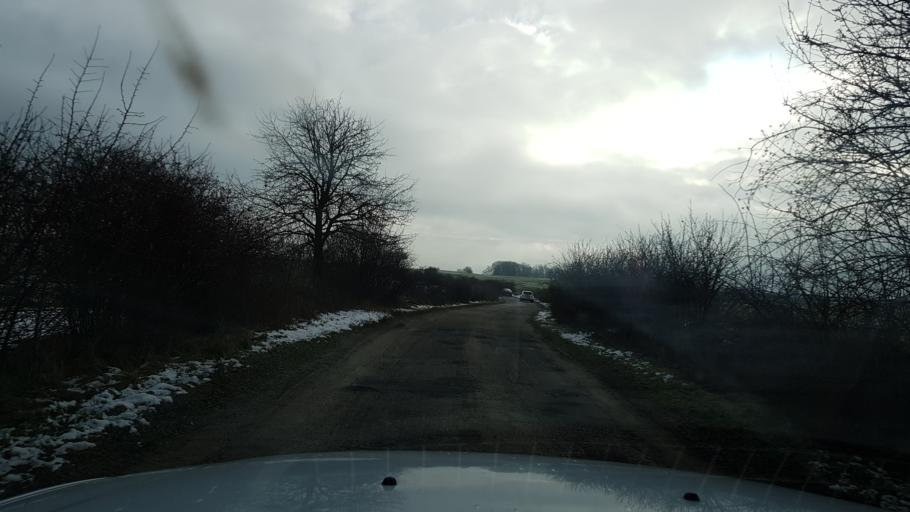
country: PL
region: West Pomeranian Voivodeship
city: Trzcinsko Zdroj
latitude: 52.9558
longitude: 14.6872
